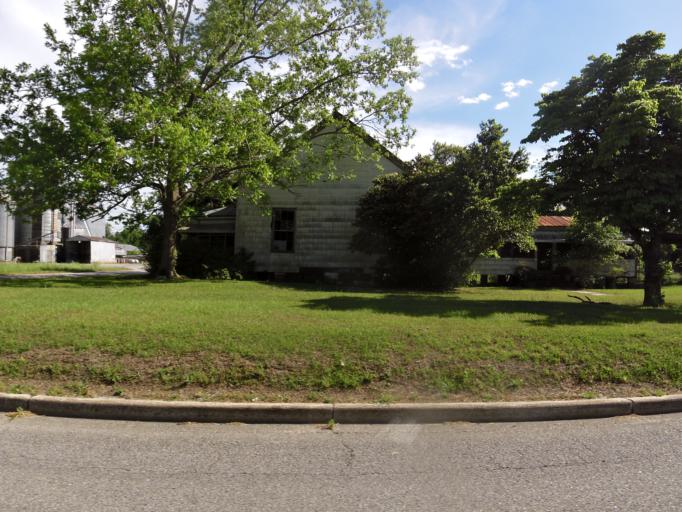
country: US
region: South Carolina
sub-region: Allendale County
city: Allendale
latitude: 33.0962
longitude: -81.2097
